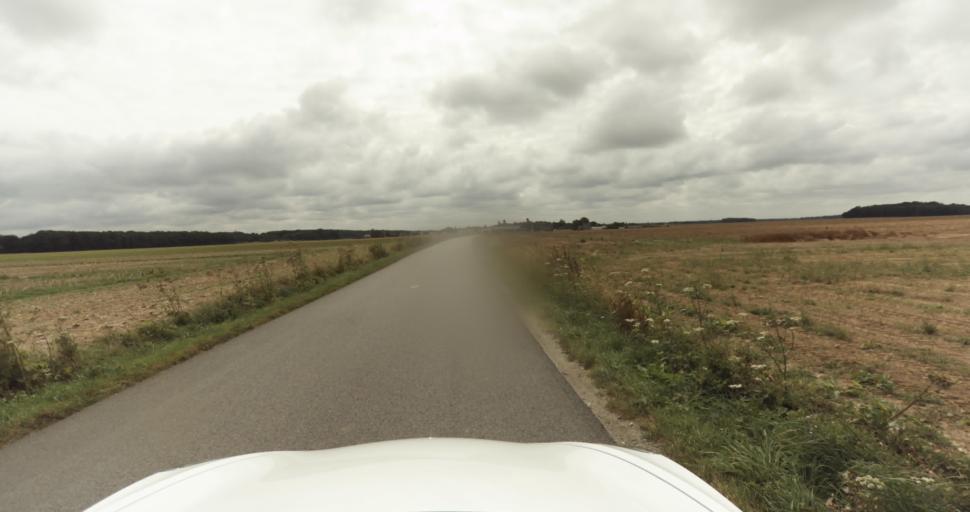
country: FR
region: Haute-Normandie
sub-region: Departement de l'Eure
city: Claville
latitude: 49.0346
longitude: 1.0288
